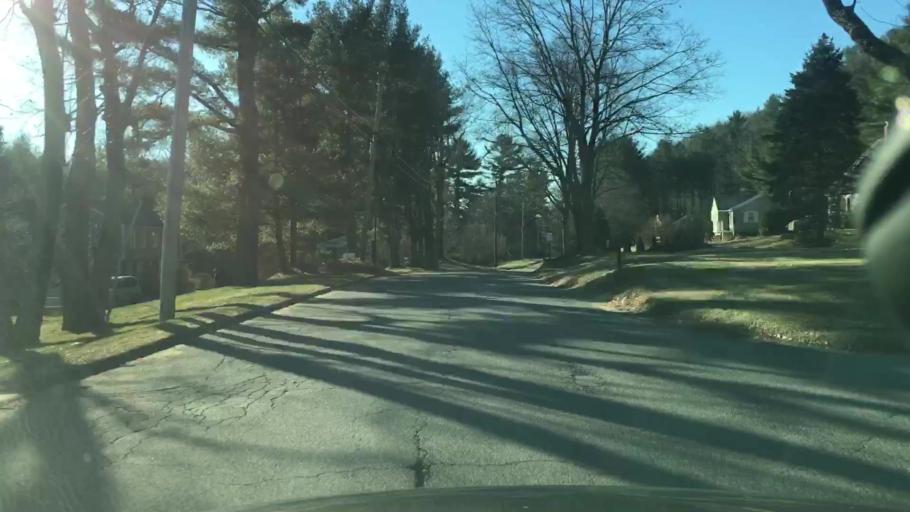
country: US
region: Connecticut
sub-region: Tolland County
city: Stafford
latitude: 41.9747
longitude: -72.2971
